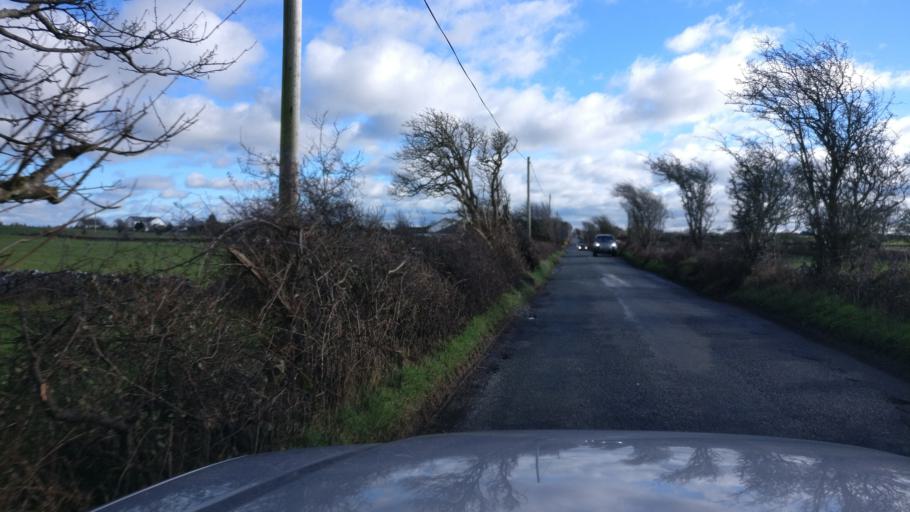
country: IE
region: Connaught
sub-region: County Galway
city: Oranmore
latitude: 53.2679
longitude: -8.8736
